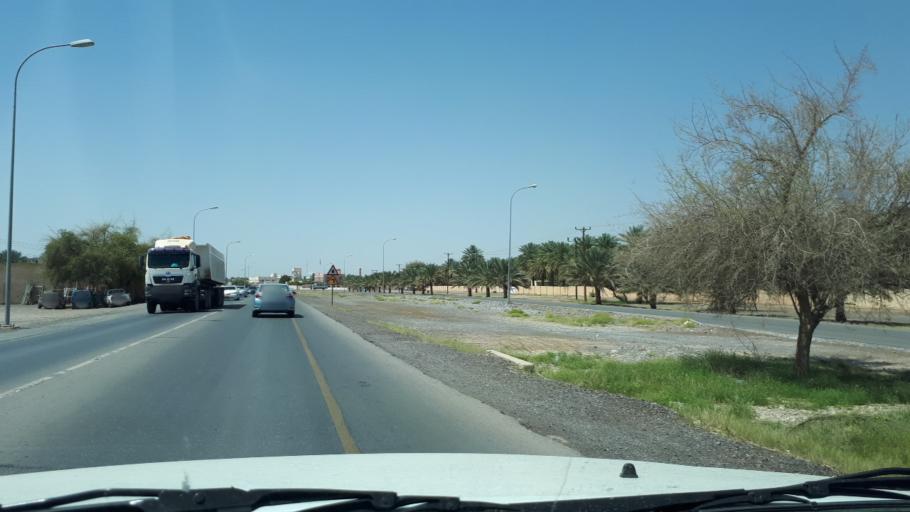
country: OM
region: Muhafazat ad Dakhiliyah
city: Bahla'
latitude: 22.9906
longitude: 57.3118
